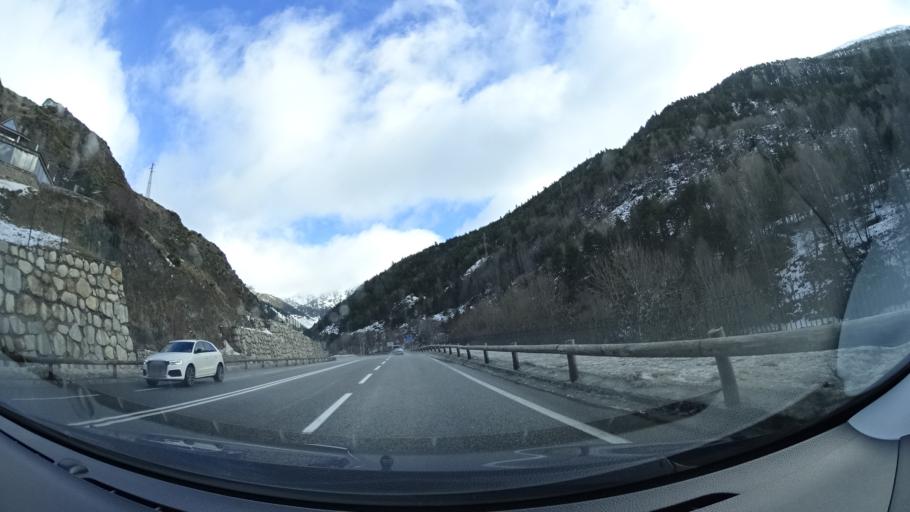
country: AD
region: Canillo
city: El Tarter
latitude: 42.5784
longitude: 1.6314
